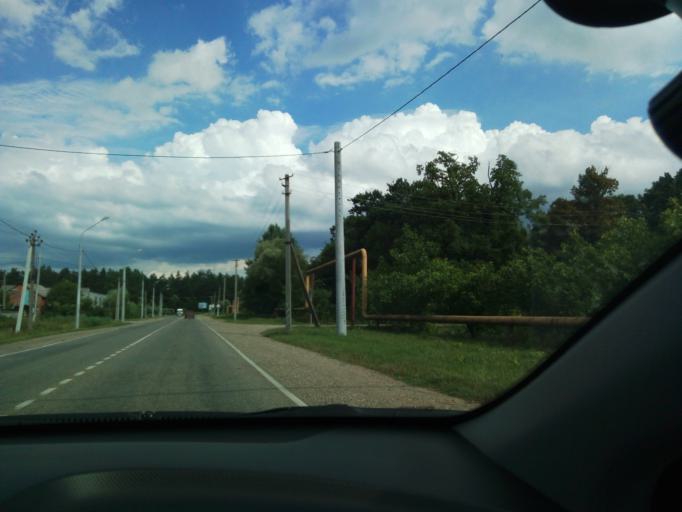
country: RU
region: Krasnodarskiy
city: Apsheronsk
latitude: 44.4374
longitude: 39.7610
